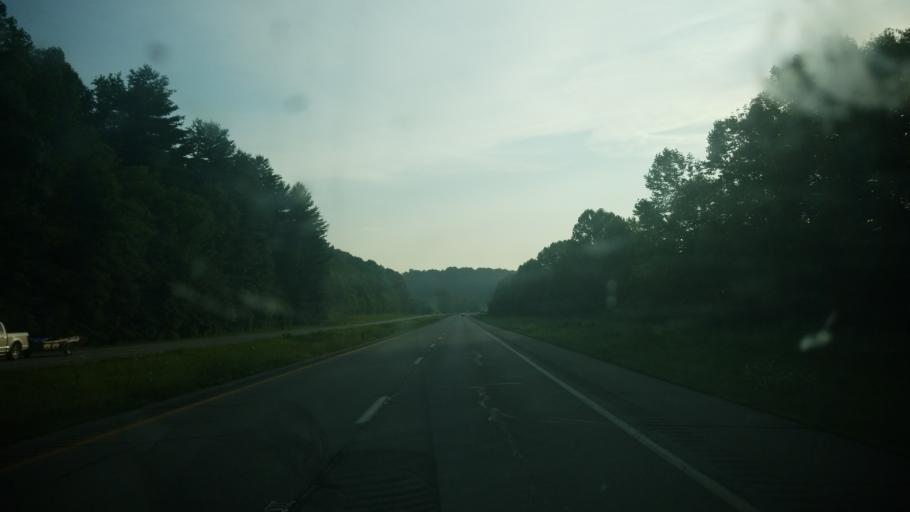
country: US
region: Ohio
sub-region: Pike County
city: Piketon
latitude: 39.0611
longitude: -83.0886
